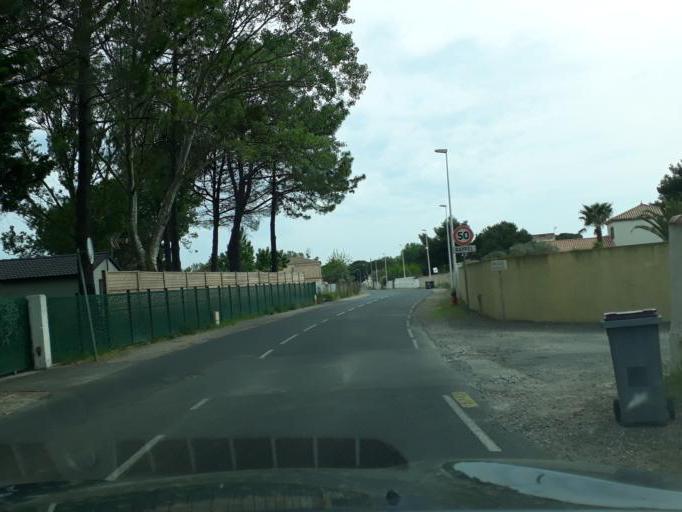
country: FR
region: Languedoc-Roussillon
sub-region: Departement de l'Herault
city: Agde
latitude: 43.2837
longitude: 3.4693
